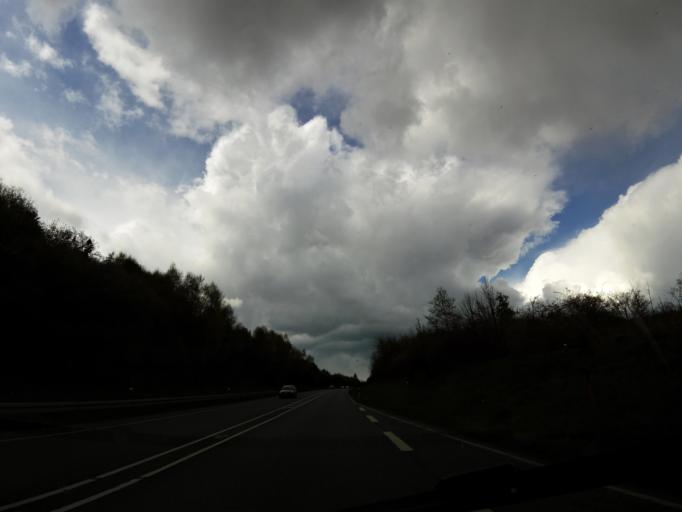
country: DE
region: Lower Saxony
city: Langelsheim
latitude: 51.9325
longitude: 10.3162
